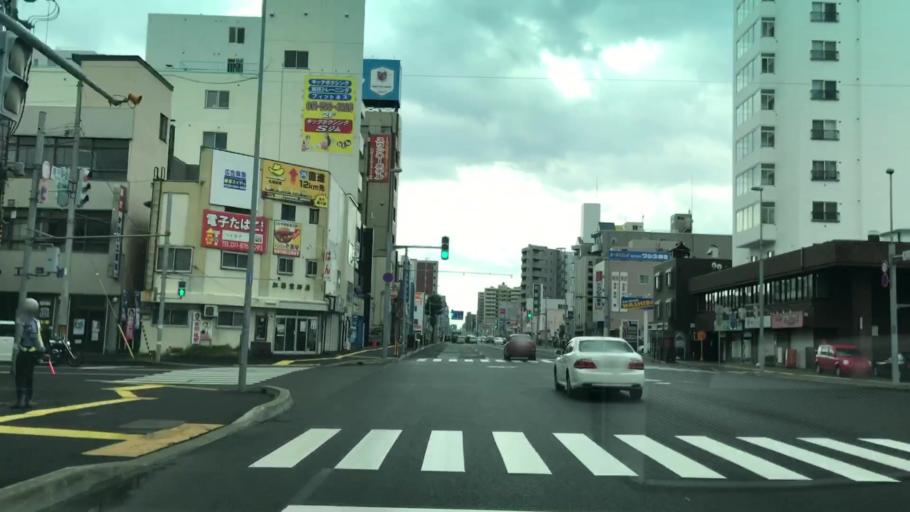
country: JP
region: Hokkaido
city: Sapporo
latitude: 43.0536
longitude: 141.3679
